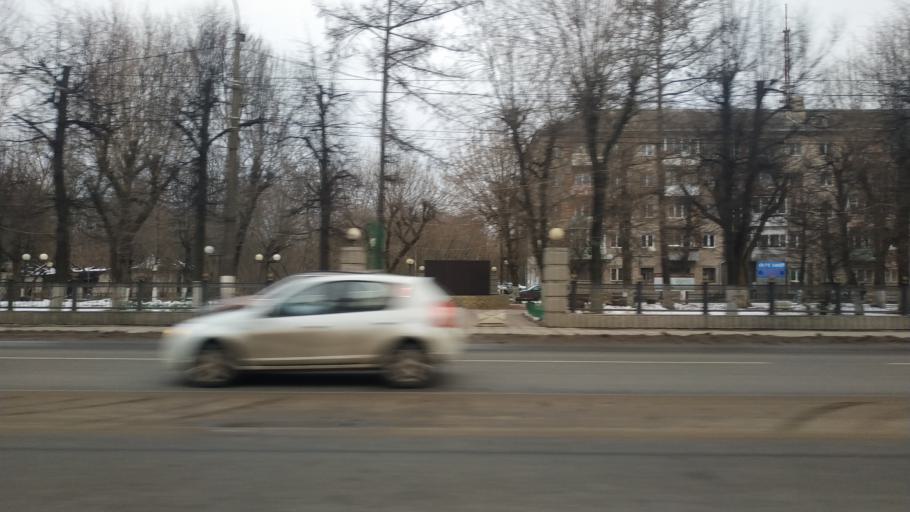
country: RU
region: Tverskaya
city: Tver
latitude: 56.8564
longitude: 35.9272
